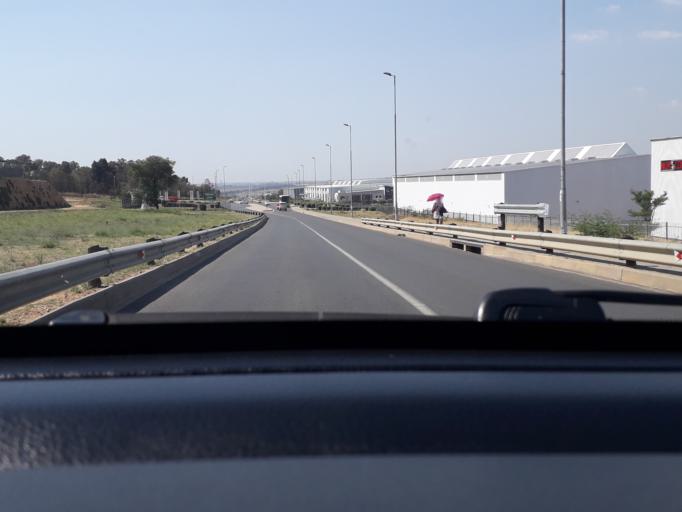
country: ZA
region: Gauteng
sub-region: City of Johannesburg Metropolitan Municipality
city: Modderfontein
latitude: -26.1026
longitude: 28.1386
